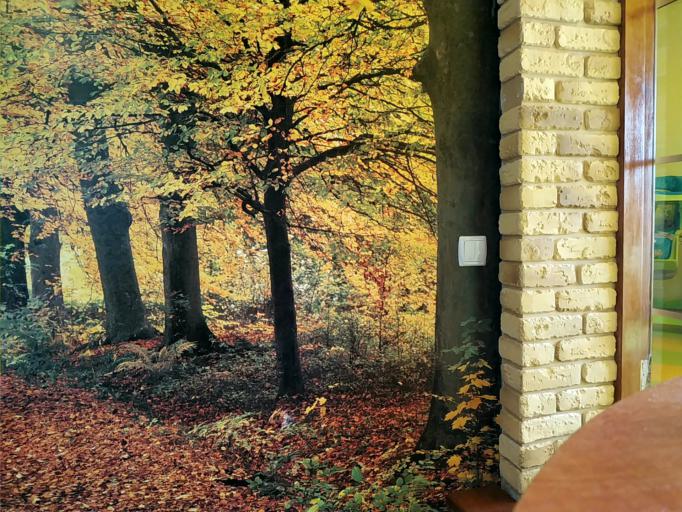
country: RU
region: Novgorod
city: Staraya Russa
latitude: 57.8374
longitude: 31.4658
